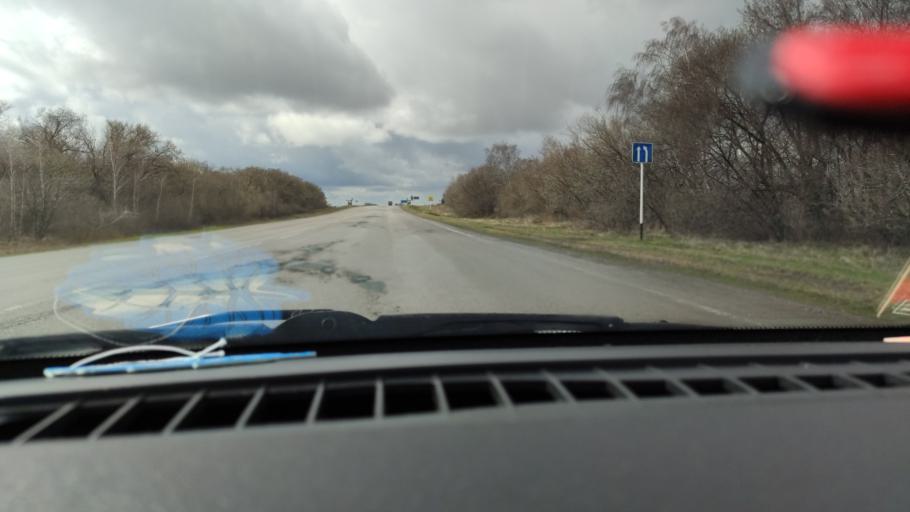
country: RU
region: Samara
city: Yelkhovka
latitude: 54.0113
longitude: 50.2623
